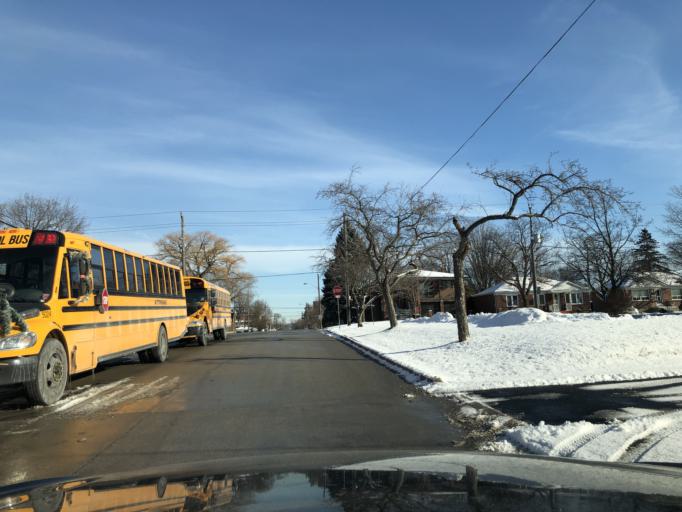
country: CA
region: Ontario
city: Etobicoke
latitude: 43.7092
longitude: -79.5183
